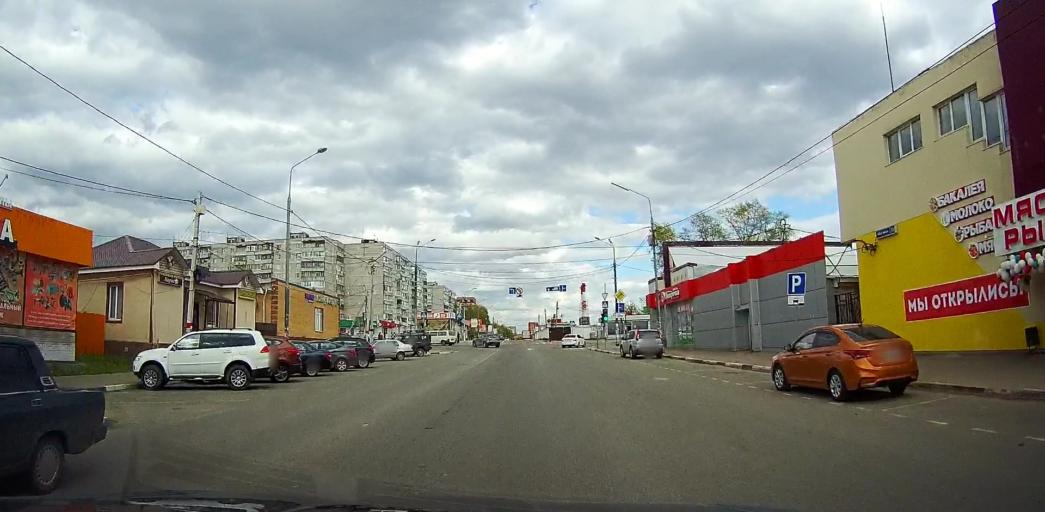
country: RU
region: Moskovskaya
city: Pavlovskiy Posad
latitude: 55.7755
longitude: 38.6508
